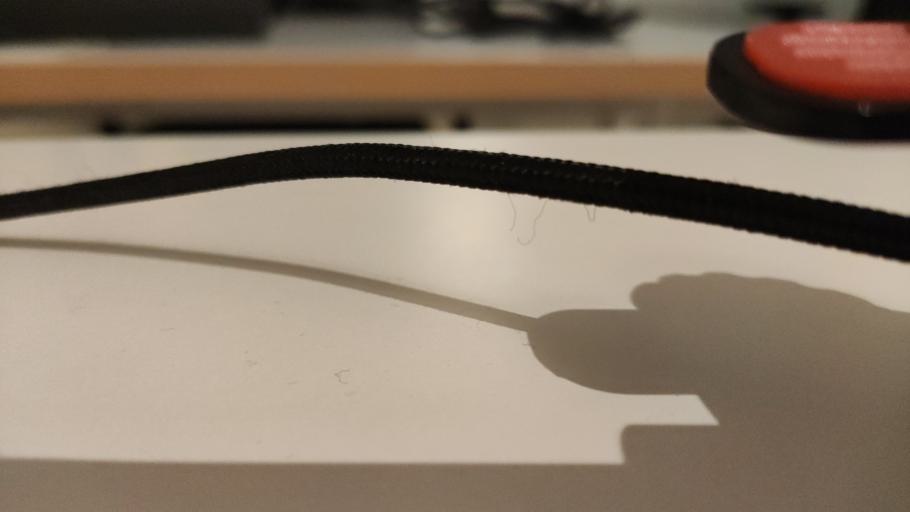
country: RU
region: Moskovskaya
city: Il'inskiy Pogost
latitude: 55.4990
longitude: 38.8738
